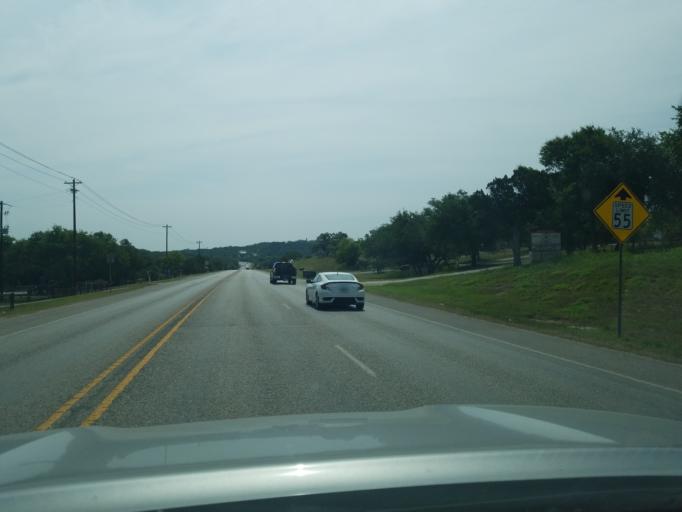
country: US
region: Texas
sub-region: Comal County
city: Bulverde
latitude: 29.7970
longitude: -98.4536
